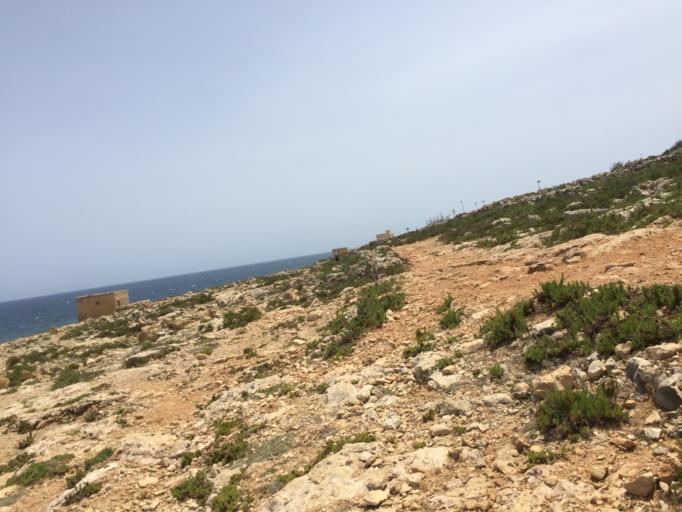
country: MT
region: Ix-Xghajra
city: Xghajra
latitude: 35.8798
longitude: 14.5612
